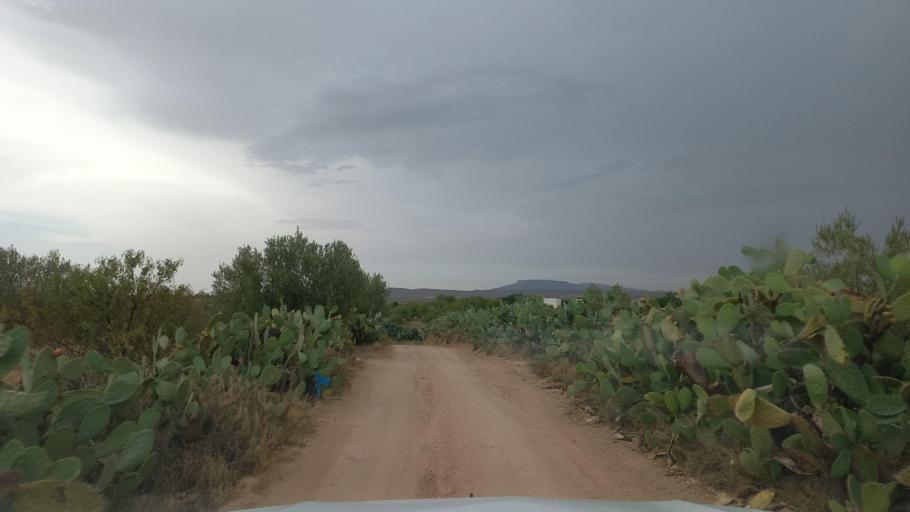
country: TN
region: Al Qasrayn
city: Kasserine
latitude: 35.2393
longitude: 9.0246
